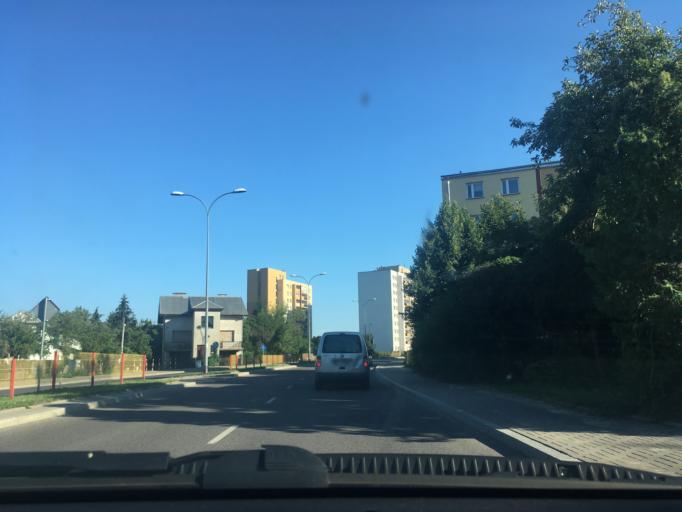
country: PL
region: Podlasie
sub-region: Bialystok
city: Bialystok
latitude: 53.1389
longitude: 23.1512
